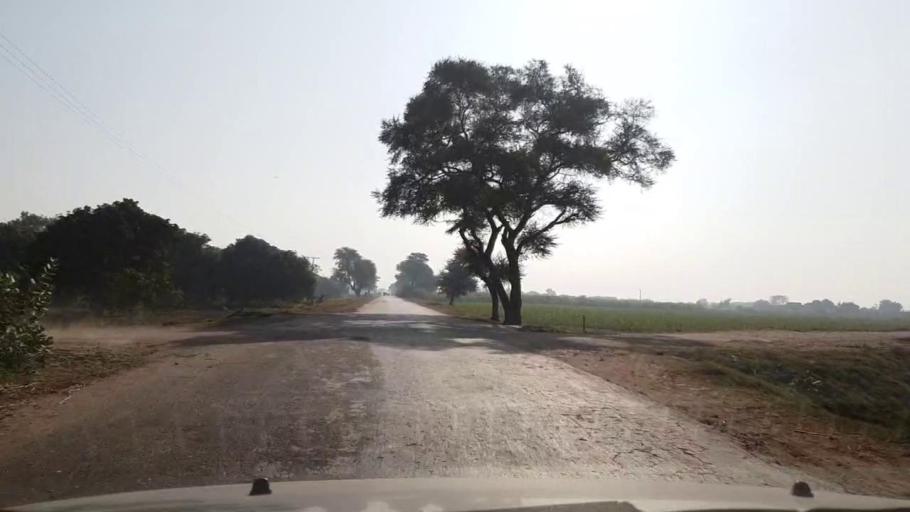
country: PK
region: Sindh
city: Matiari
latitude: 25.5595
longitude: 68.5298
